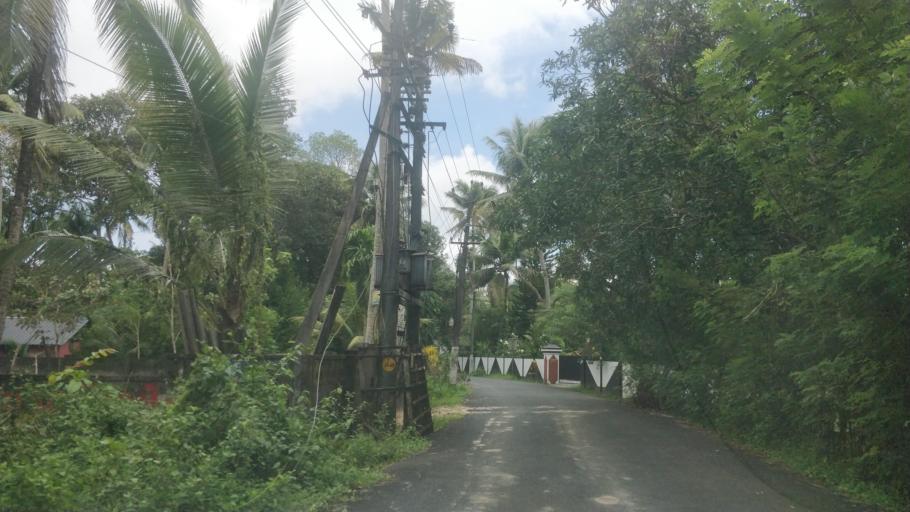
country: IN
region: Kerala
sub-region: Alappuzha
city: Shertallai
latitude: 9.6597
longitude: 76.3719
